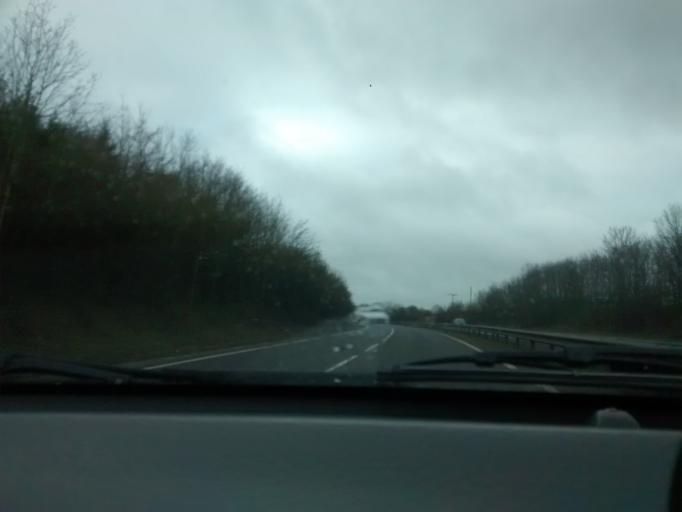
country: GB
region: England
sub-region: Suffolk
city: Stowmarket
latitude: 52.1920
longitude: 1.0155
